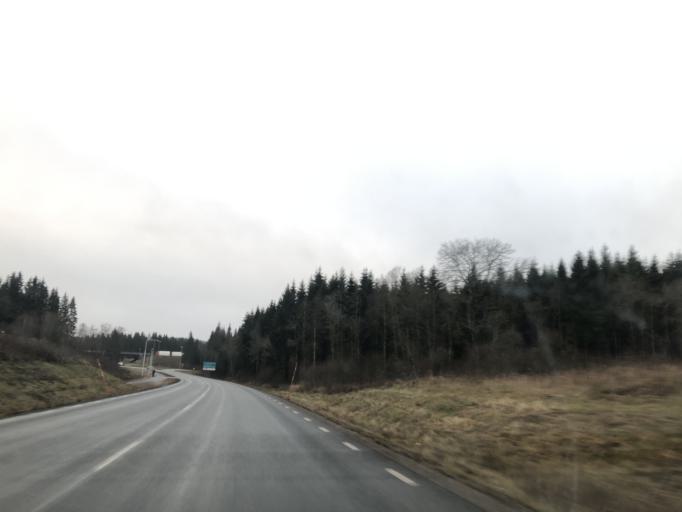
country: SE
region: Vaestra Goetaland
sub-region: Ulricehamns Kommun
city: Ulricehamn
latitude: 57.8232
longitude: 13.2864
